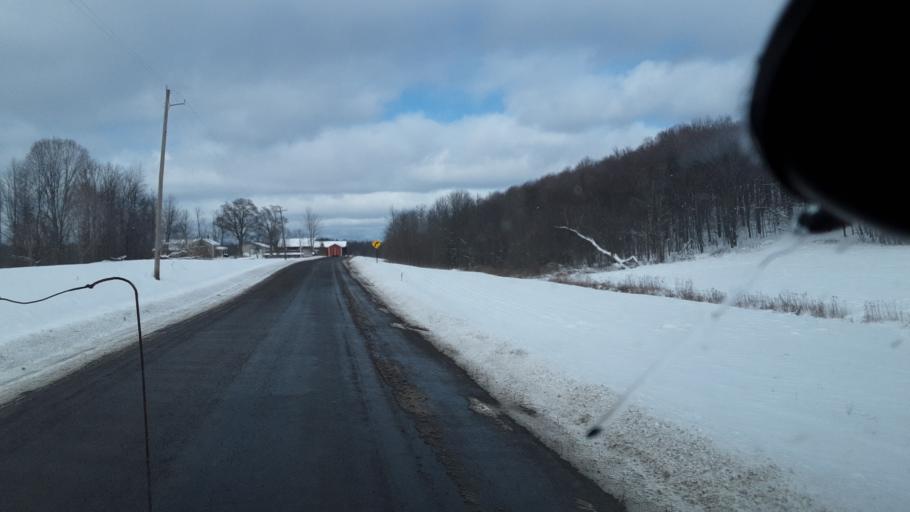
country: US
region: New York
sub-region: Wayne County
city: Lyons
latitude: 43.1087
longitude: -77.0457
